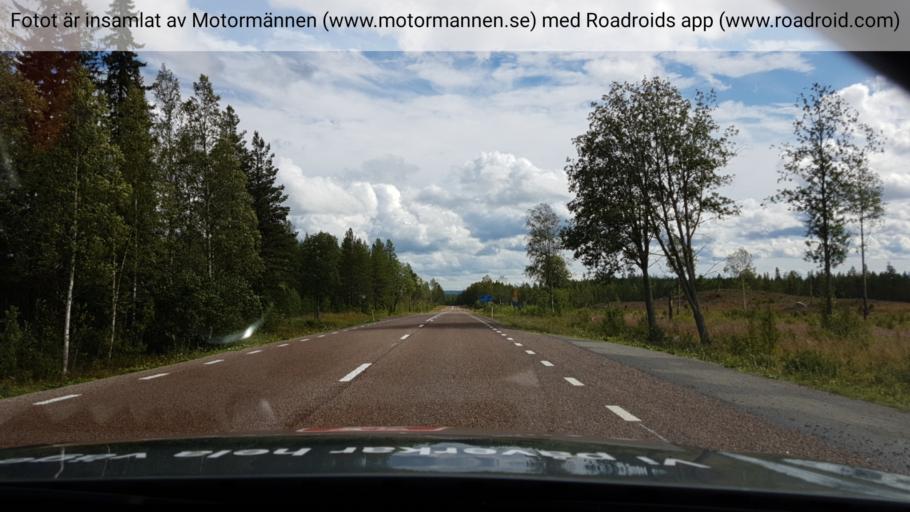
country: SE
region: Jaemtland
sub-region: OEstersunds Kommun
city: Brunflo
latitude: 63.1964
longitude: 15.0951
